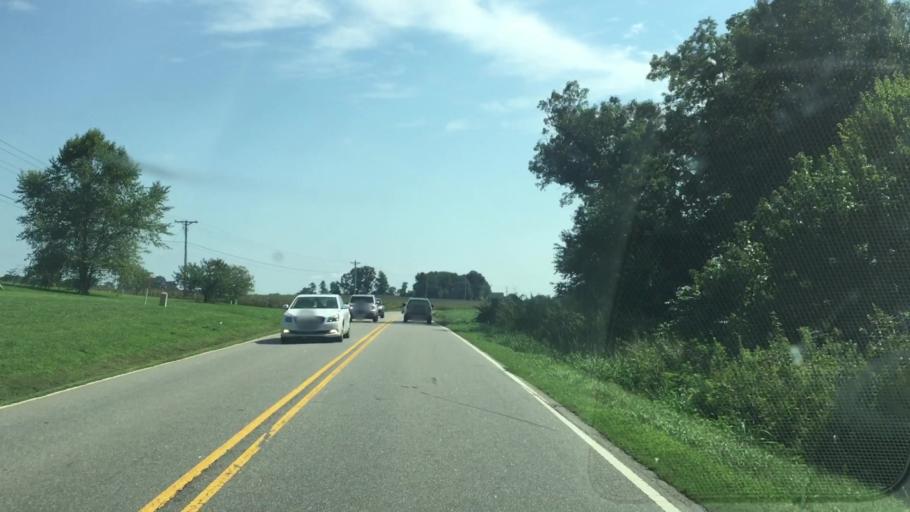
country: US
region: North Carolina
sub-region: Union County
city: Unionville
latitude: 35.1247
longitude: -80.4143
